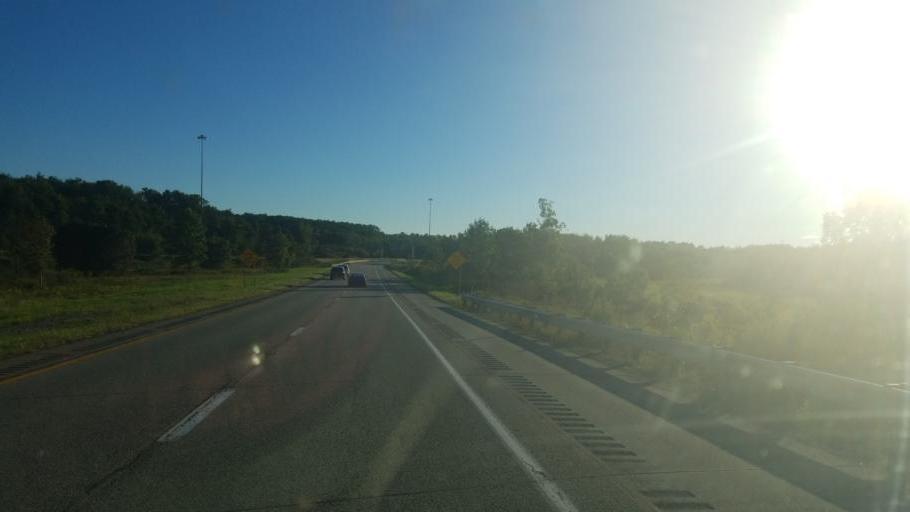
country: US
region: Pennsylvania
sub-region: Erie County
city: North East
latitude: 42.1523
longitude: -79.8990
